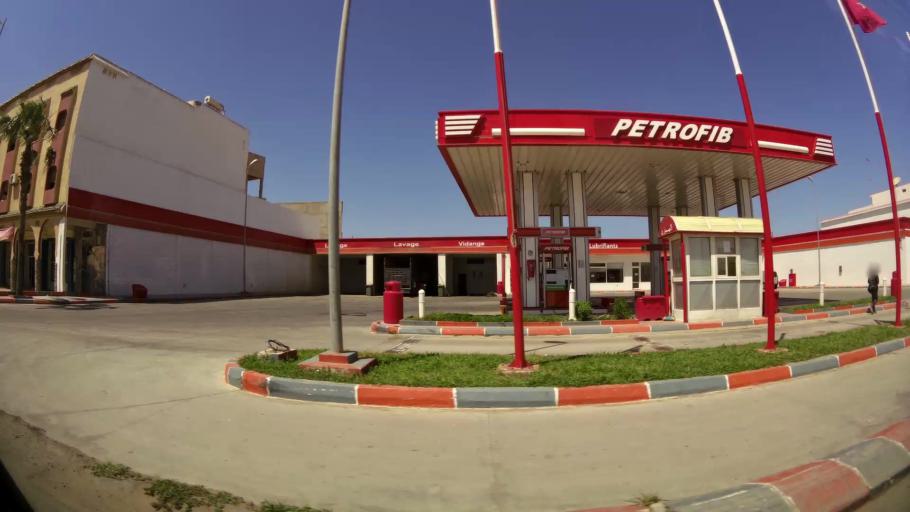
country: MA
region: Souss-Massa-Draa
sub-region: Inezgane-Ait Mellou
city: Inezgane
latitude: 30.3146
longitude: -9.5030
